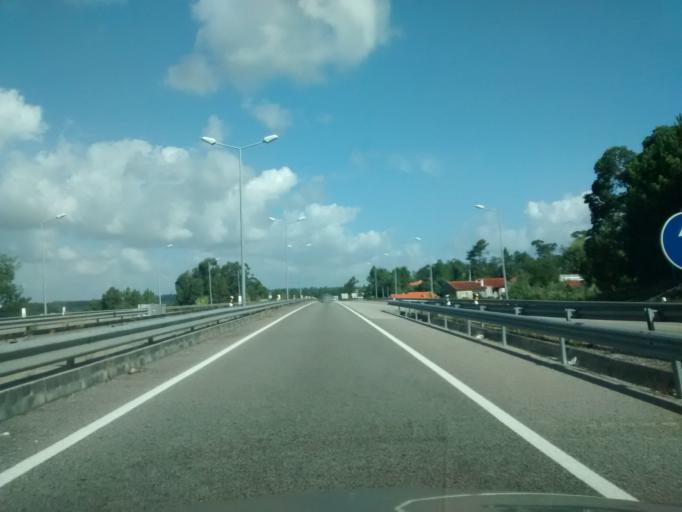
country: PT
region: Aveiro
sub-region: Oliveira do Bairro
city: Oliveira do Bairro
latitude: 40.5142
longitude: -8.5003
